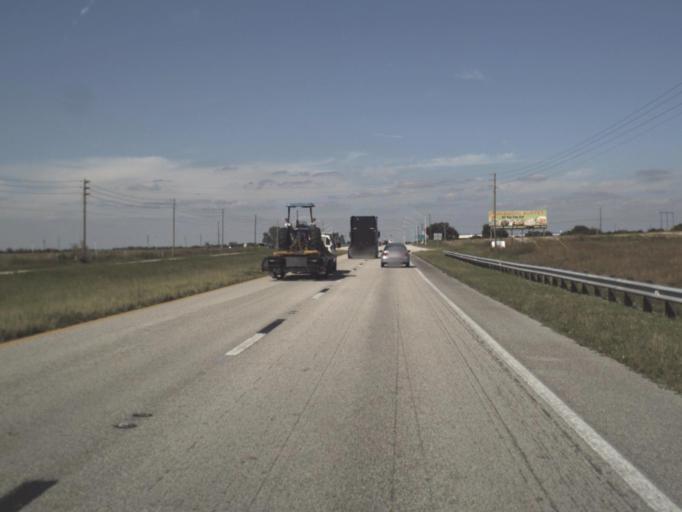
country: US
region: Florida
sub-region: Highlands County
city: Sebring
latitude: 27.4237
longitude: -81.4174
